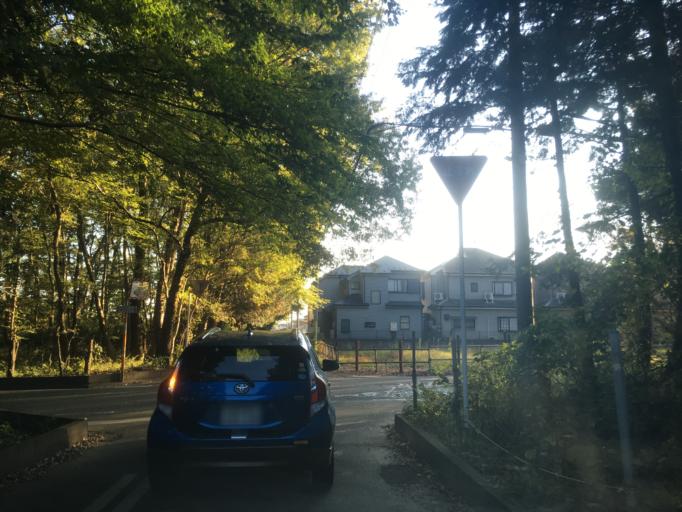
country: JP
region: Saitama
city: Tokorozawa
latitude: 35.8153
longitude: 139.4369
